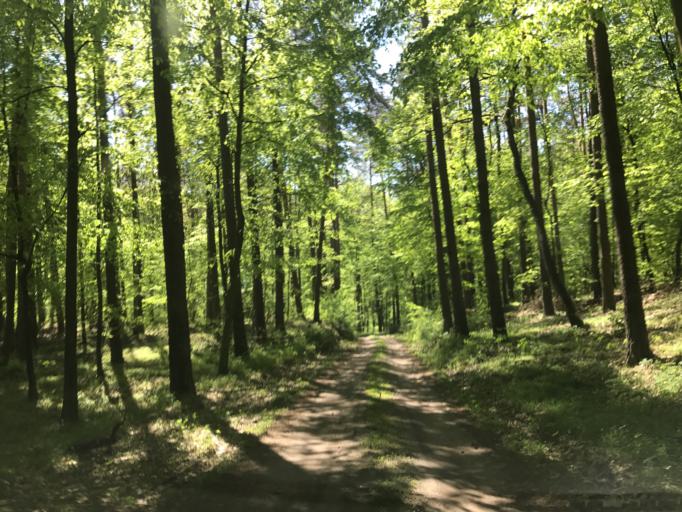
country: PL
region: Kujawsko-Pomorskie
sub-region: Powiat brodnicki
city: Gorzno
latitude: 53.2212
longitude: 19.7353
